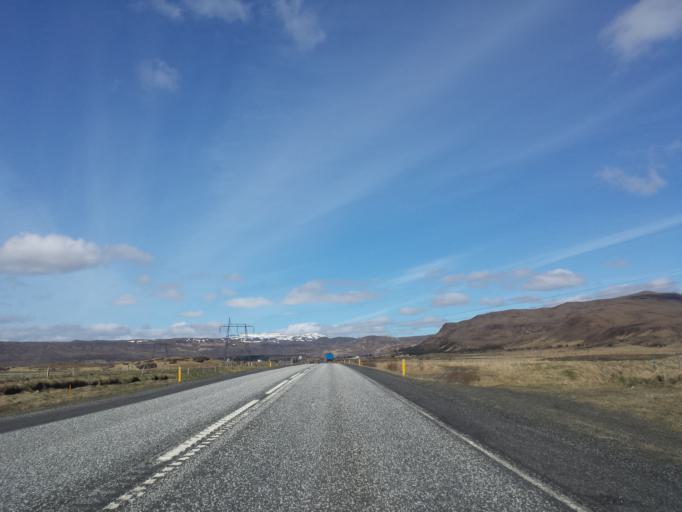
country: IS
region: South
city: Hveragerdi
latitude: 63.9802
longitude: -21.1524
